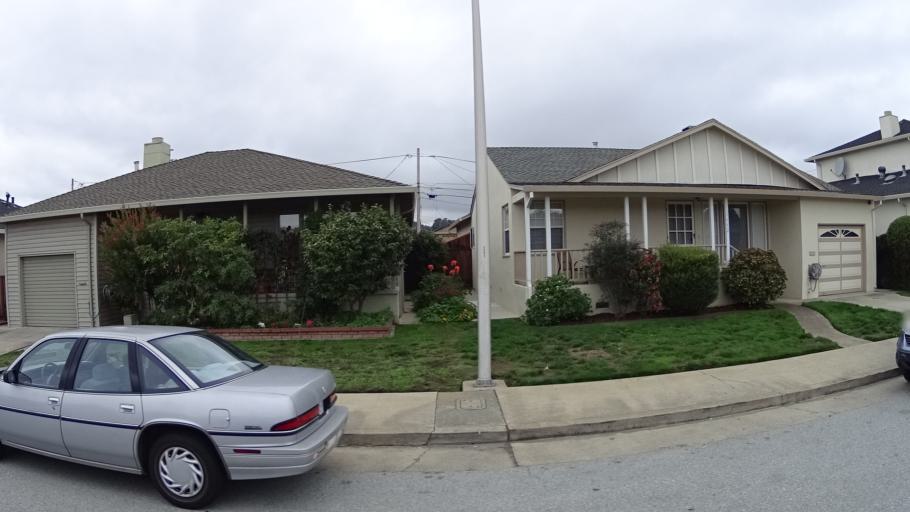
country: US
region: California
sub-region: San Mateo County
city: Belmont
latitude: 37.5362
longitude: -122.2917
